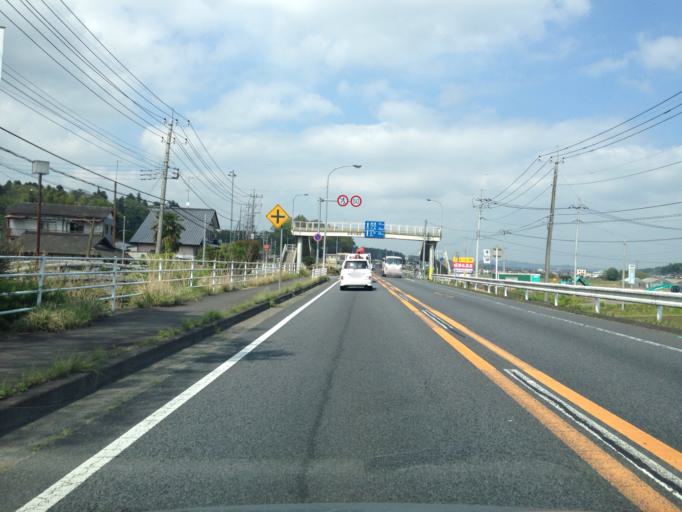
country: JP
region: Ibaraki
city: Kasama
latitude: 36.3640
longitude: 140.2051
